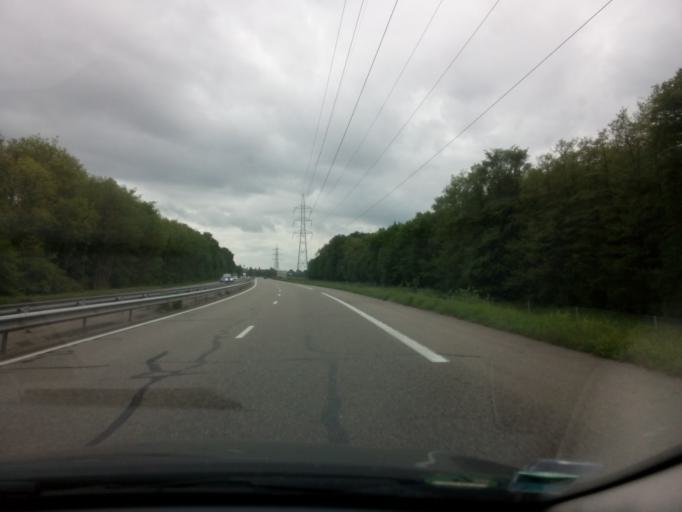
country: FR
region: Alsace
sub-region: Departement du Bas-Rhin
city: Drusenheim
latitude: 48.7580
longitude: 7.9243
